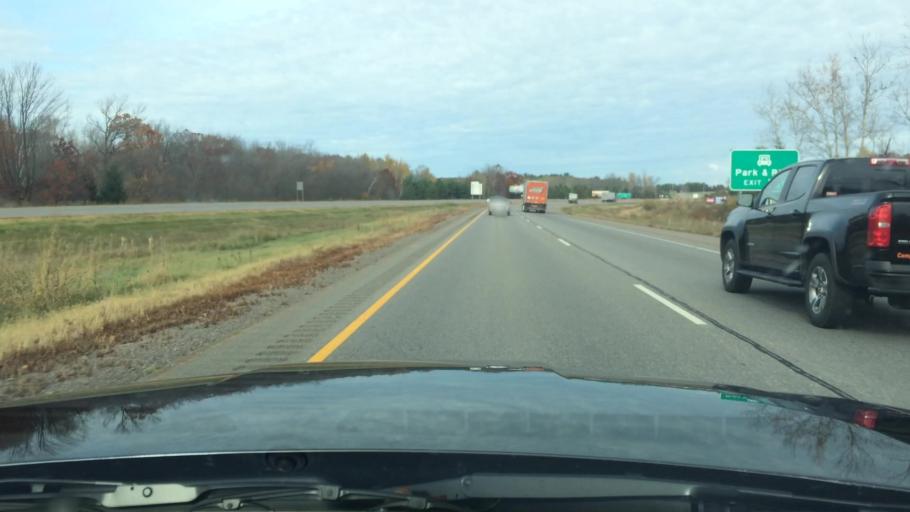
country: US
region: Wisconsin
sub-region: Marathon County
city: Mosinee
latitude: 44.8021
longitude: -89.6781
